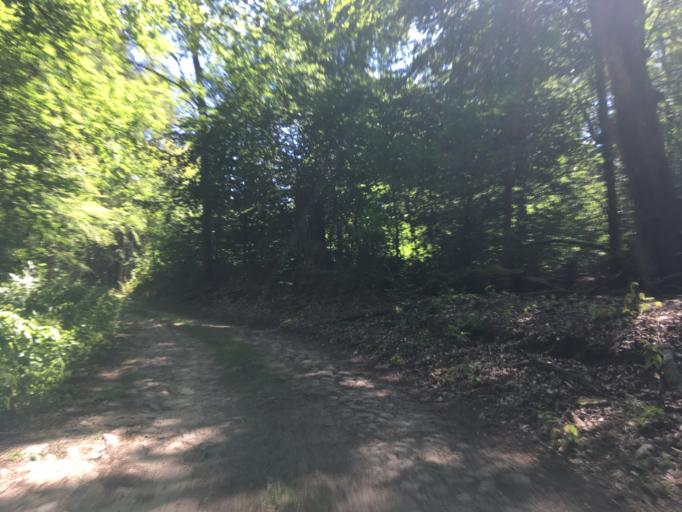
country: DE
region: Brandenburg
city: Rheinsberg
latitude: 53.1248
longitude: 13.0038
